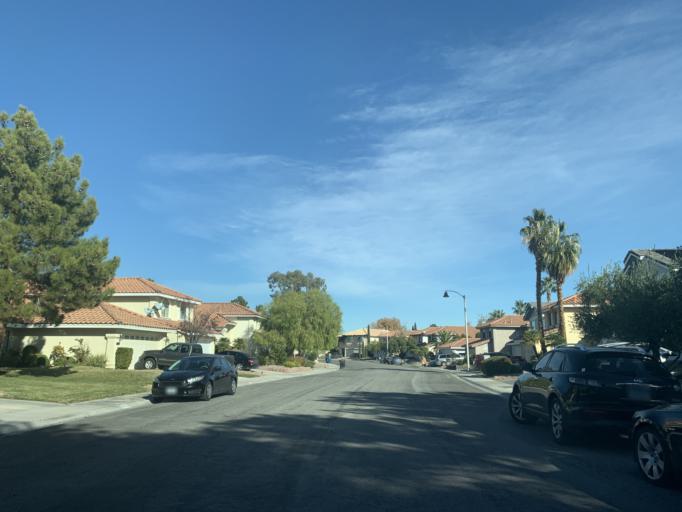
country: US
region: Nevada
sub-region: Clark County
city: Summerlin South
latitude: 36.1356
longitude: -115.2906
